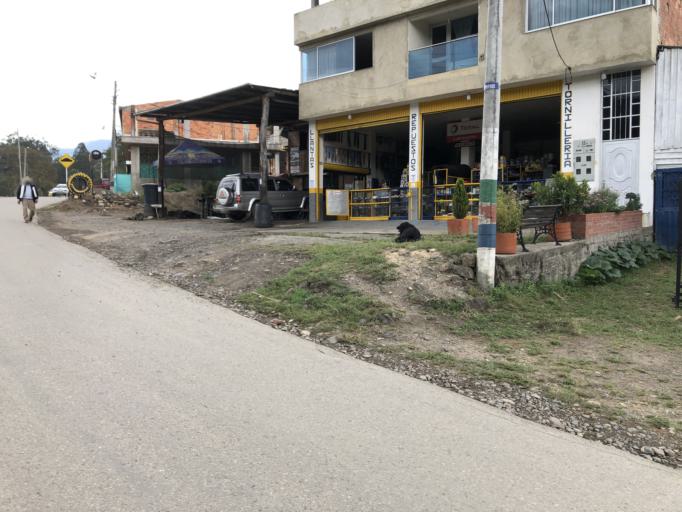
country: CO
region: Cundinamarca
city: Gacheta
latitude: 4.8163
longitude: -73.6386
